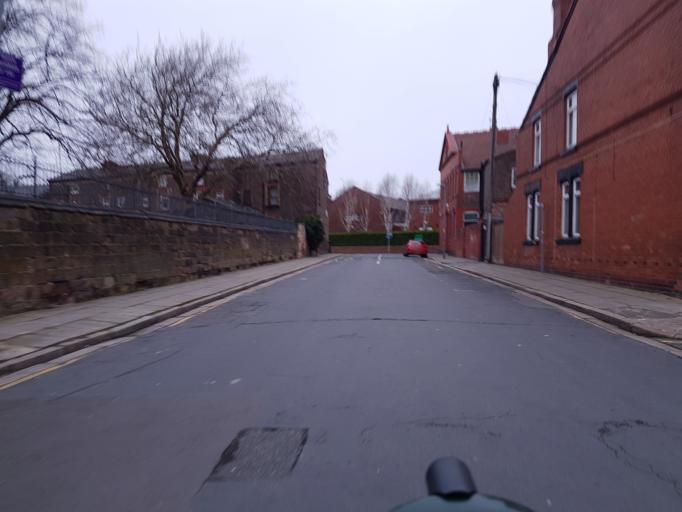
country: GB
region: England
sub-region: Liverpool
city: Liverpool
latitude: 53.4452
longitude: -2.9659
